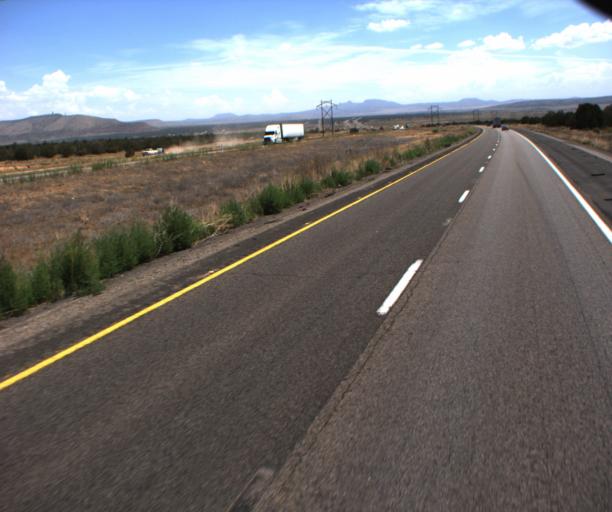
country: US
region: Arizona
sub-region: Mohave County
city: Peach Springs
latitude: 35.3024
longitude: -113.0051
